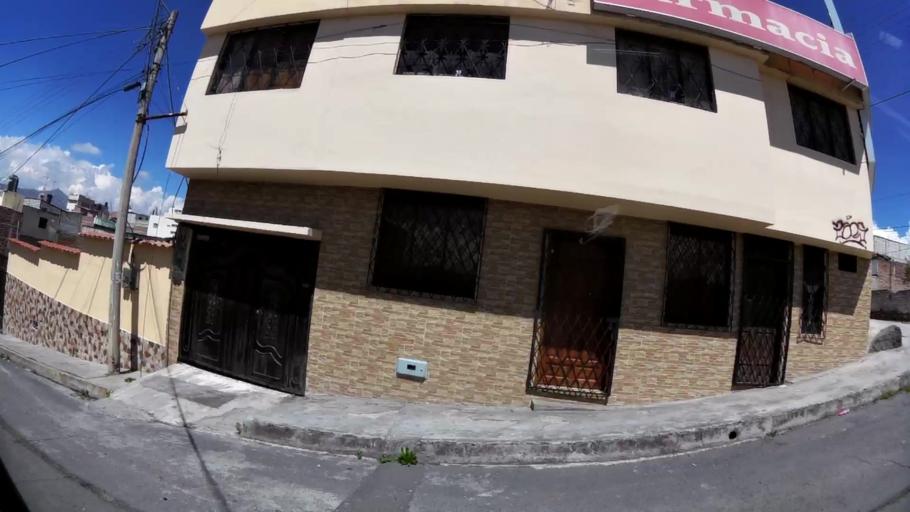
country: EC
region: Chimborazo
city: Riobamba
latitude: -1.6617
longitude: -78.6466
